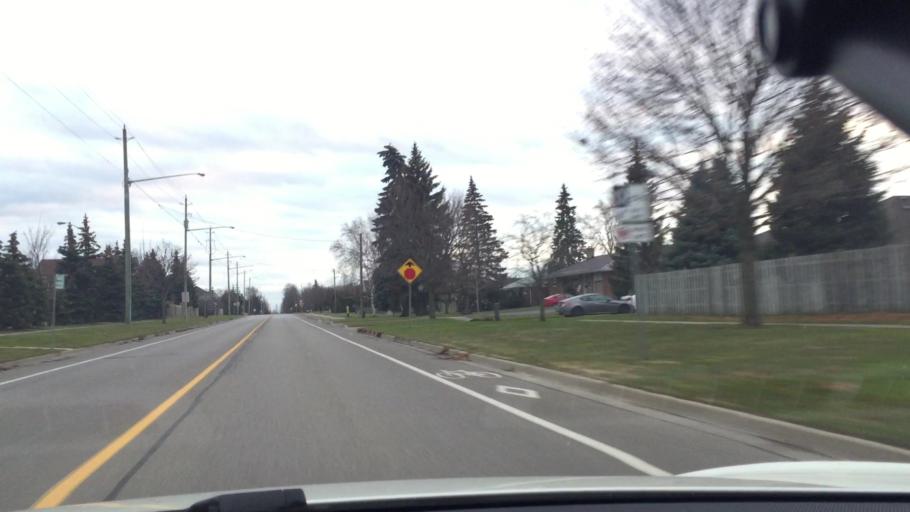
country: CA
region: Ontario
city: Oshawa
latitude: 43.9047
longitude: -78.7856
